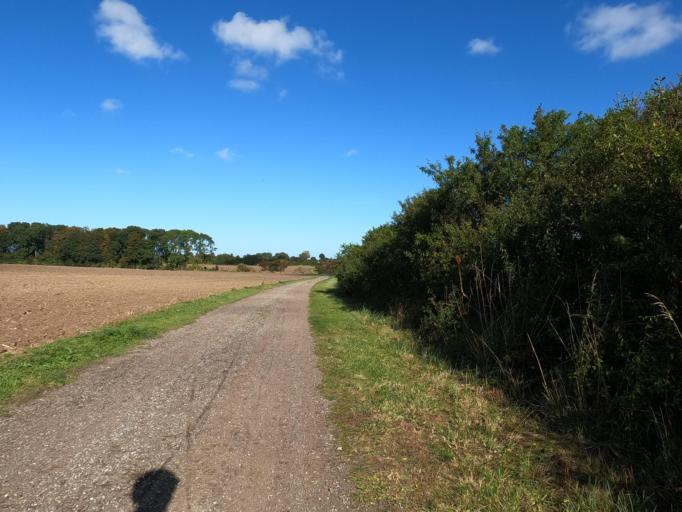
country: DE
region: Schleswig-Holstein
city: Neukirchen
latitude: 54.3161
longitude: 11.0739
